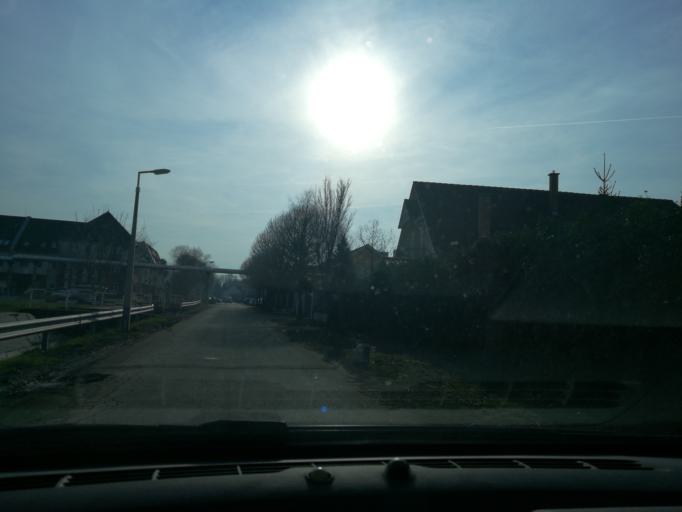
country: HU
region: Szabolcs-Szatmar-Bereg
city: Nyiregyhaza
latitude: 47.9575
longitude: 21.7316
